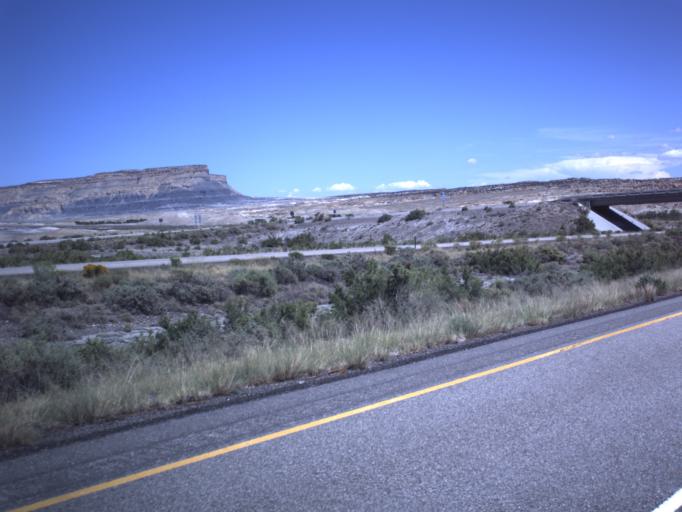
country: US
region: Utah
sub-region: Emery County
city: Ferron
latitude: 38.8109
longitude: -111.2127
